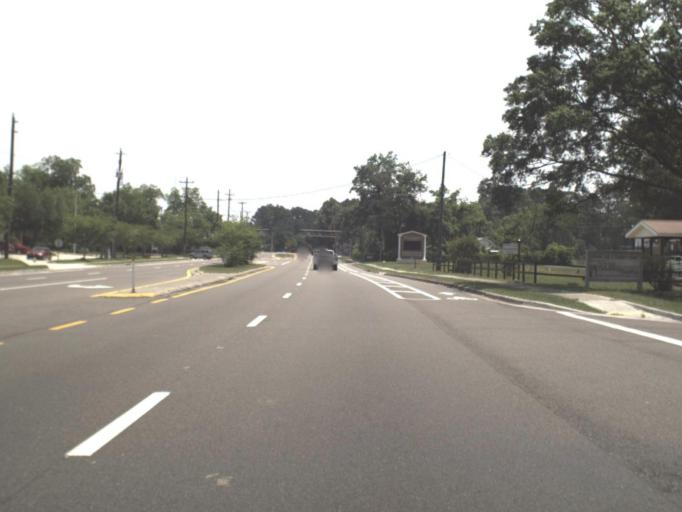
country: US
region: Florida
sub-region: Nassau County
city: Yulee
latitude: 30.6300
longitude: -81.6092
